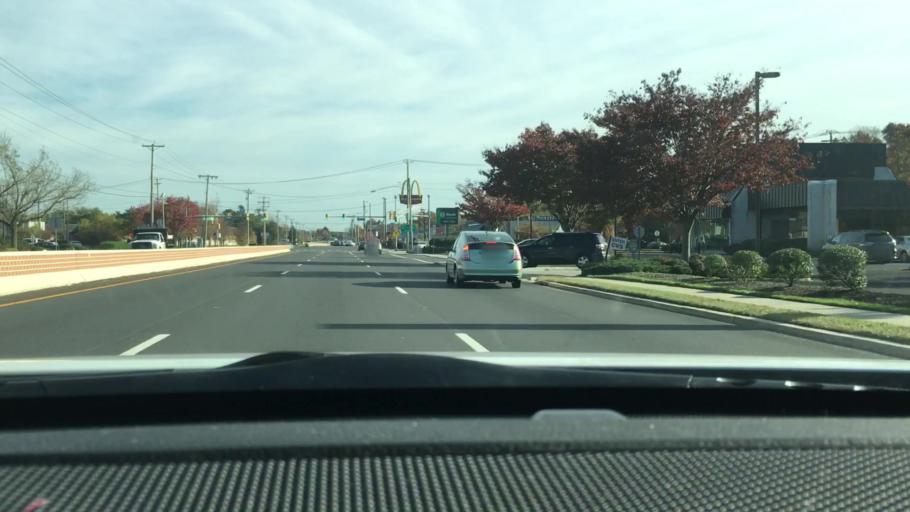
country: US
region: New Jersey
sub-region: Atlantic County
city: Absecon
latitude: 39.4327
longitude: -74.5123
